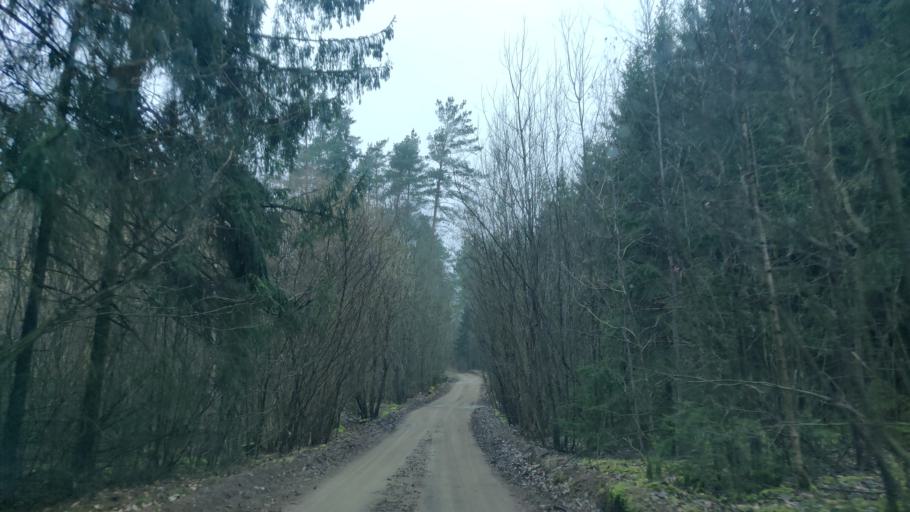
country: LT
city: Trakai
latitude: 54.5571
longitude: 24.9371
